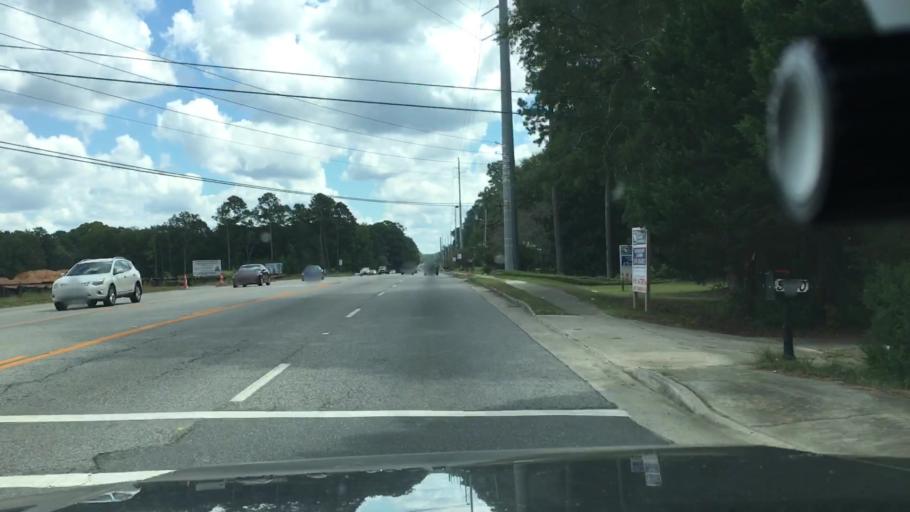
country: US
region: Georgia
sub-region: Bibb County
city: West Point
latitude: 32.8797
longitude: -83.7560
